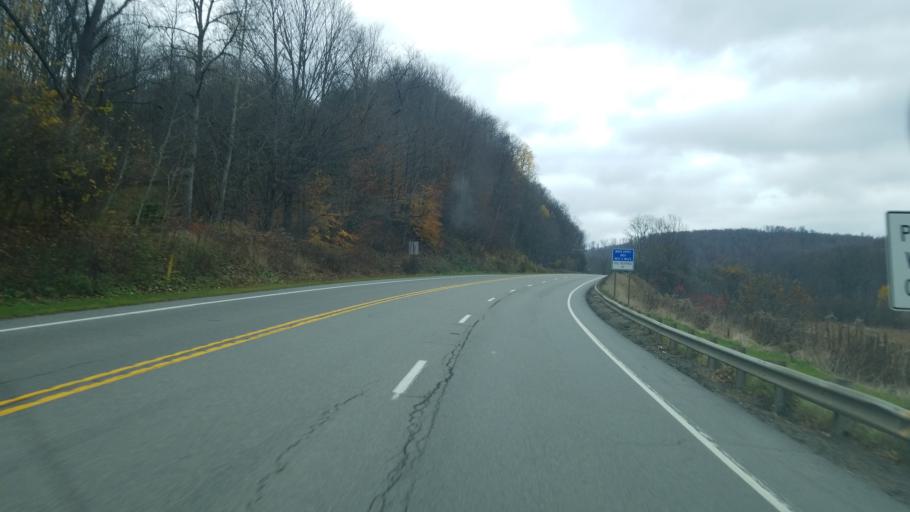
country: US
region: Pennsylvania
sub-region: McKean County
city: Smethport
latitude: 41.7060
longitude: -78.5929
